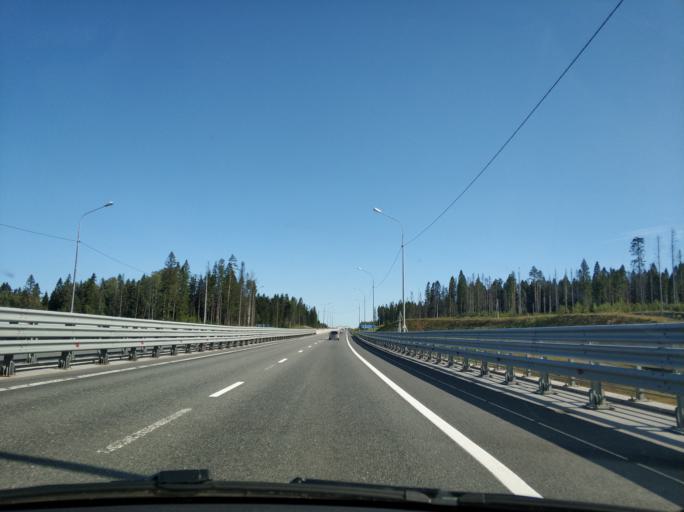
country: RU
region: Leningrad
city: Sosnovo
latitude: 60.4594
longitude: 30.1963
